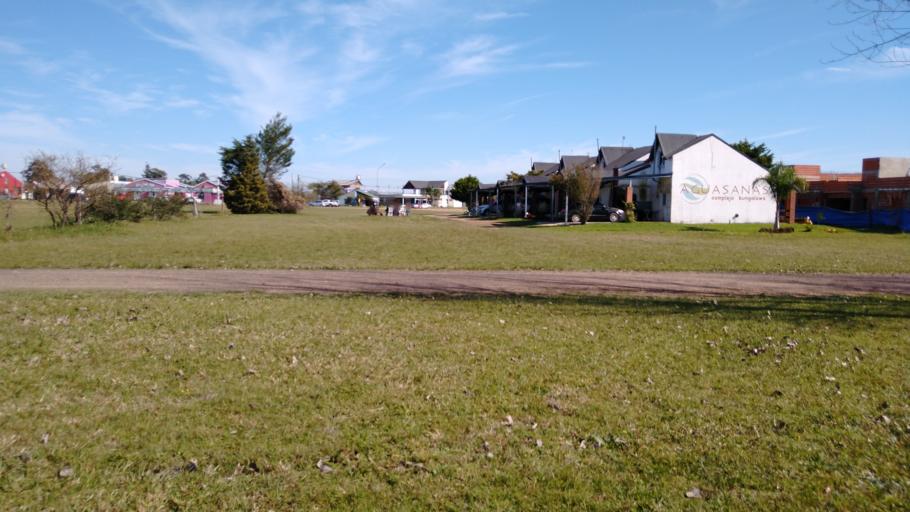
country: AR
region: Entre Rios
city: Chajari
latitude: -30.7439
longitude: -58.0103
